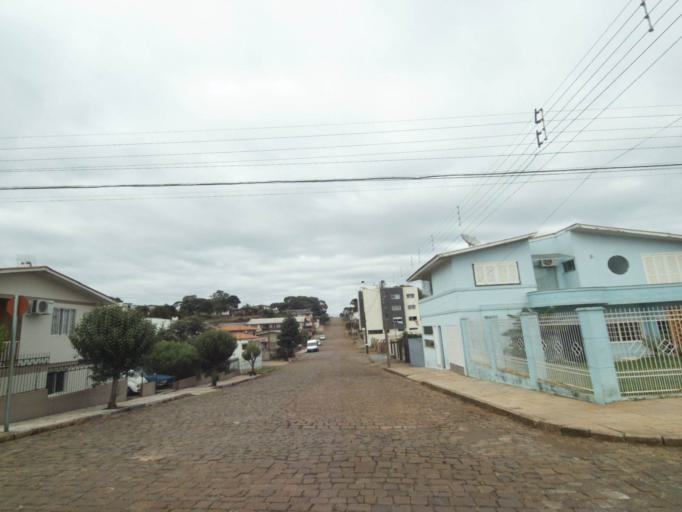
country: BR
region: Rio Grande do Sul
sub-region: Lagoa Vermelha
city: Lagoa Vermelha
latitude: -28.2157
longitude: -51.5160
